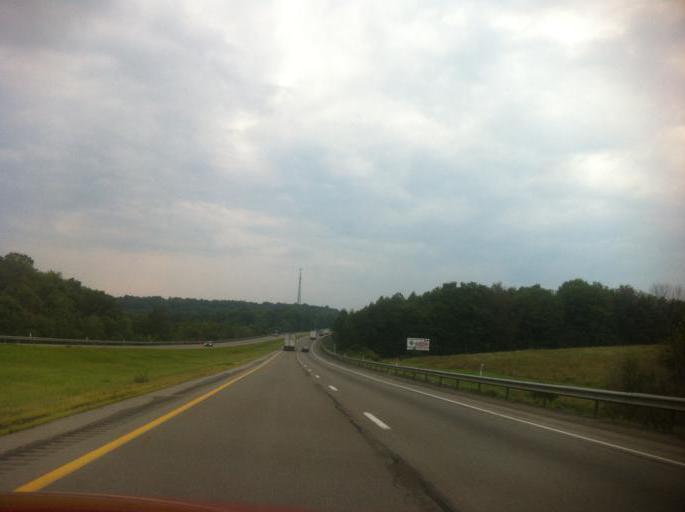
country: US
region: Pennsylvania
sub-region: Jefferson County
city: Brookville
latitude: 41.1824
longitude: -79.1500
